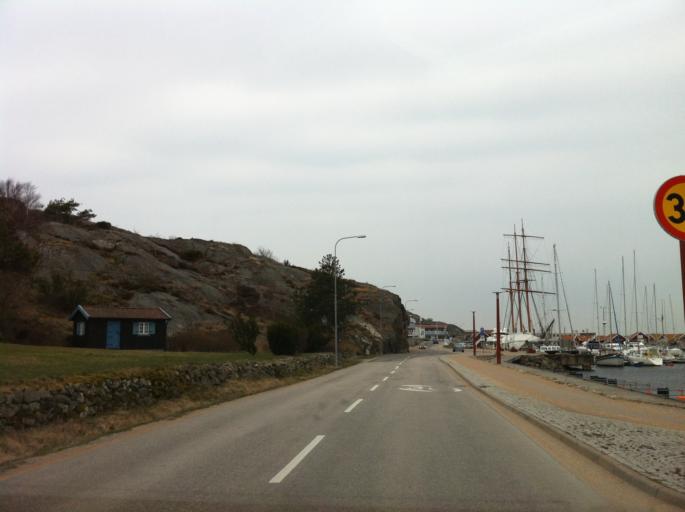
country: SE
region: Vaestra Goetaland
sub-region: Orust
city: Henan
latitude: 58.1556
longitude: 11.7054
